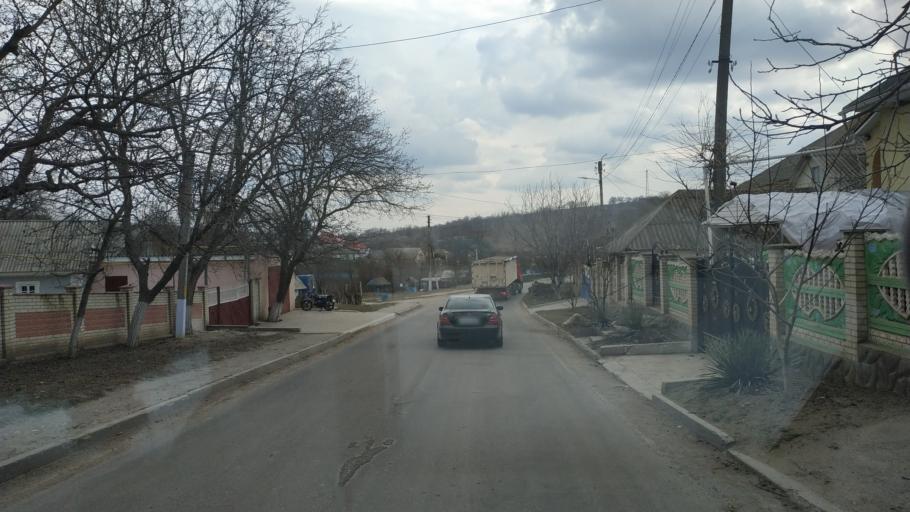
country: MD
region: Anenii Noi
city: Varnita
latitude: 46.8450
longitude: 29.3573
